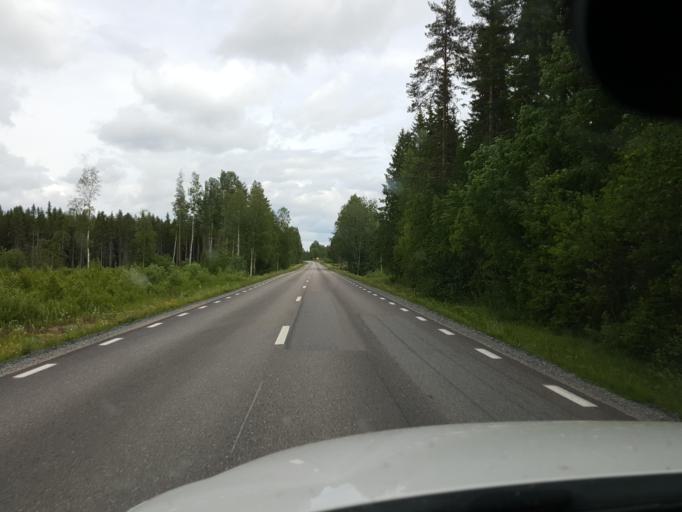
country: SE
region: Gaevleborg
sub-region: Ljusdals Kommun
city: Farila
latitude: 61.7963
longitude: 15.7076
